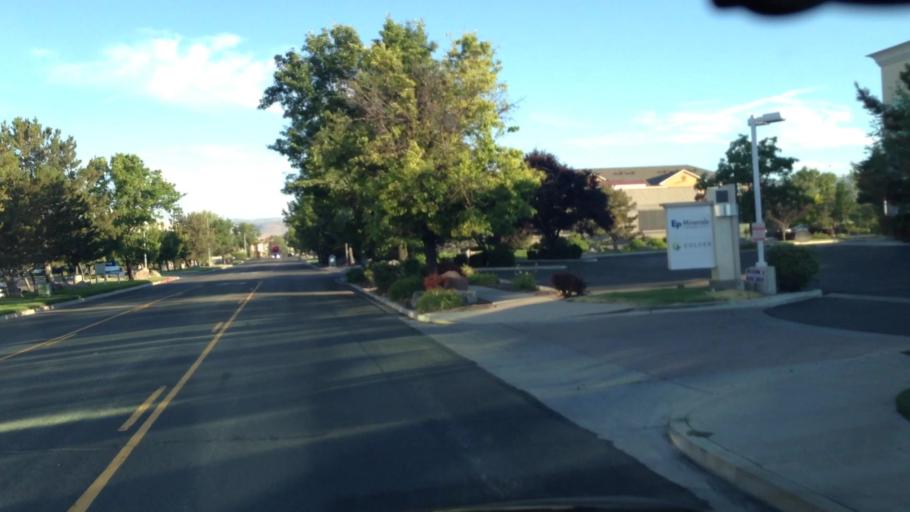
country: US
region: Nevada
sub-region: Washoe County
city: Sparks
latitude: 39.4425
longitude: -119.7624
